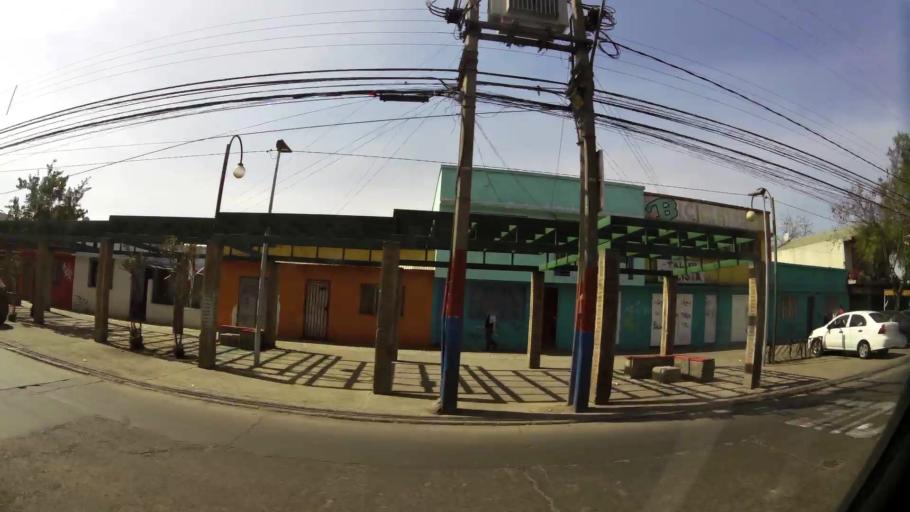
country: CL
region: Santiago Metropolitan
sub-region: Provincia de Santiago
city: Lo Prado
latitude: -33.4388
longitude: -70.7527
